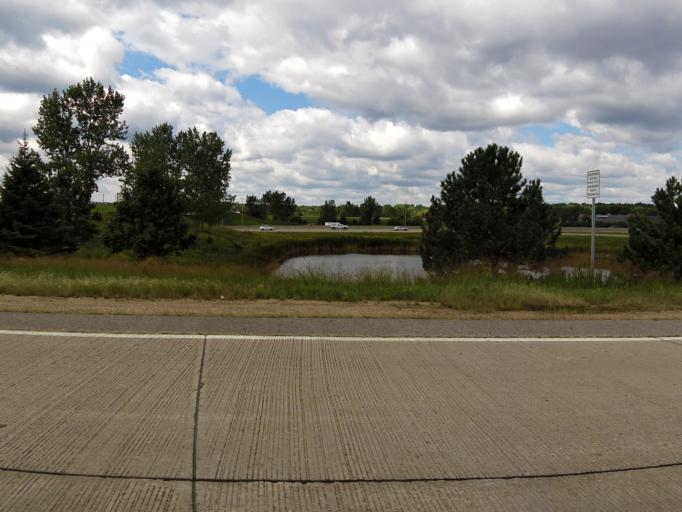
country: US
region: Minnesota
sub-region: Dakota County
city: Burnsville
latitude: 44.7148
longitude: -93.2812
